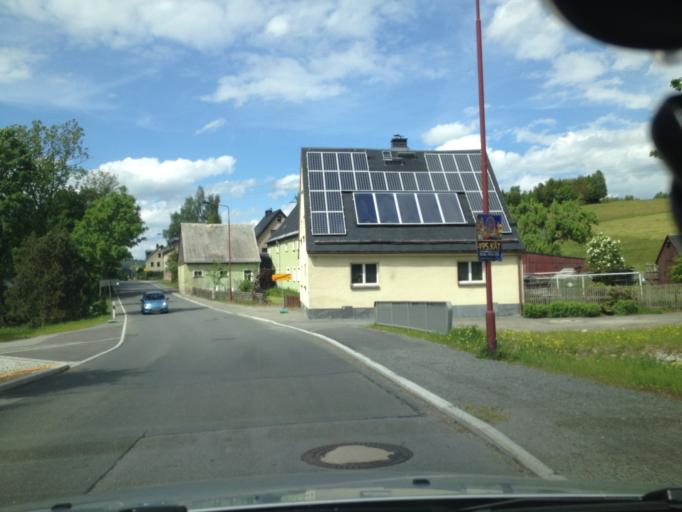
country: DE
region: Saxony
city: Barenstein
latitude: 50.5223
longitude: 12.9965
